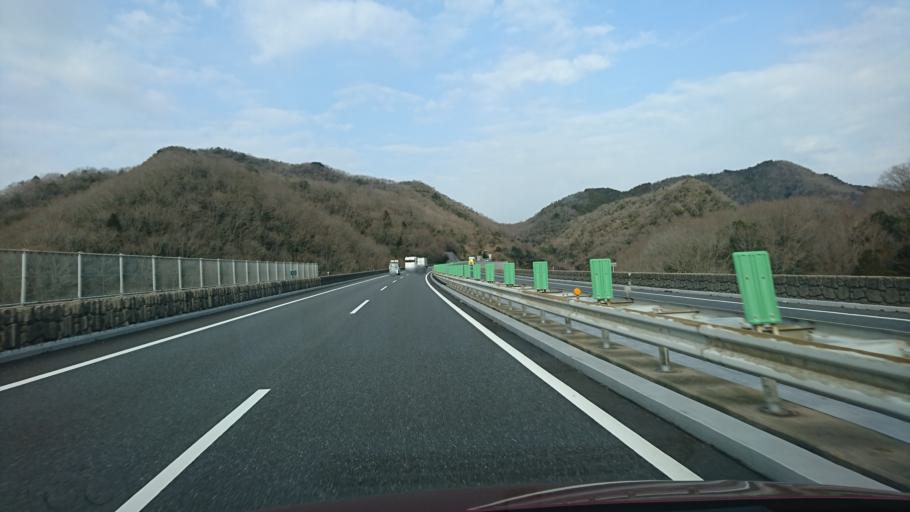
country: JP
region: Hyogo
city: Kariya
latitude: 34.7837
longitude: 134.2197
